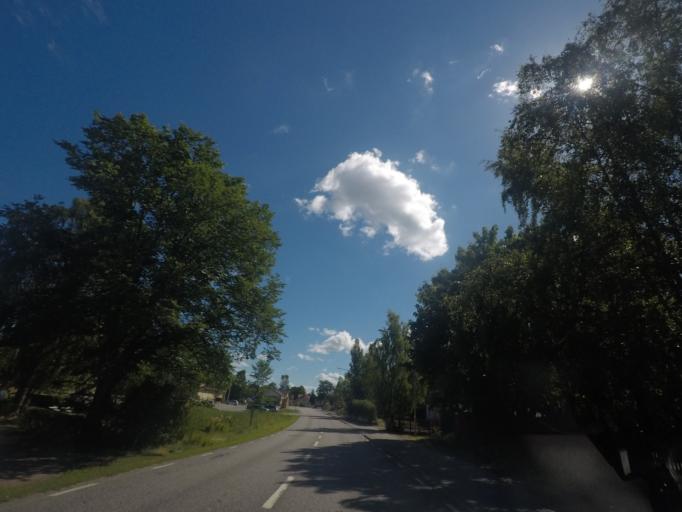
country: SE
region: Stockholm
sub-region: Norrtalje Kommun
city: Nykvarn
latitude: 59.8756
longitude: 18.0441
